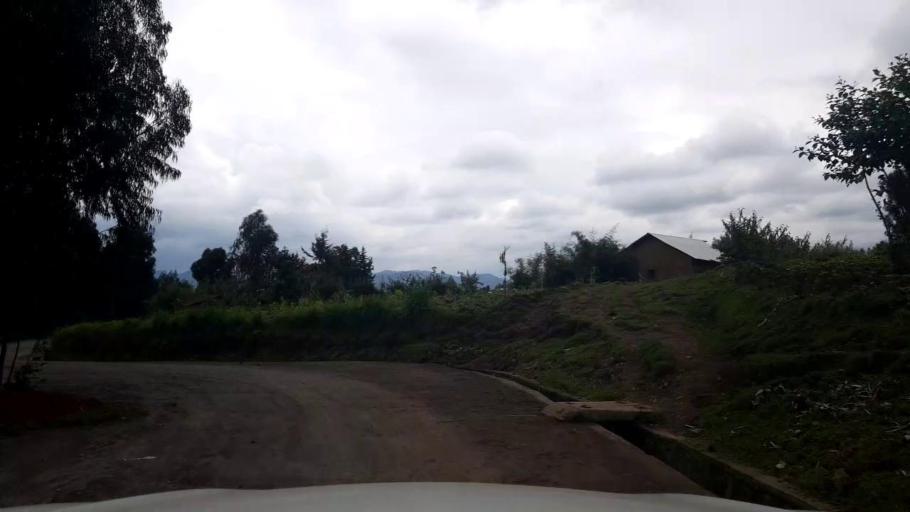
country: RW
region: Northern Province
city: Musanze
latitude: -1.5258
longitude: 29.5311
